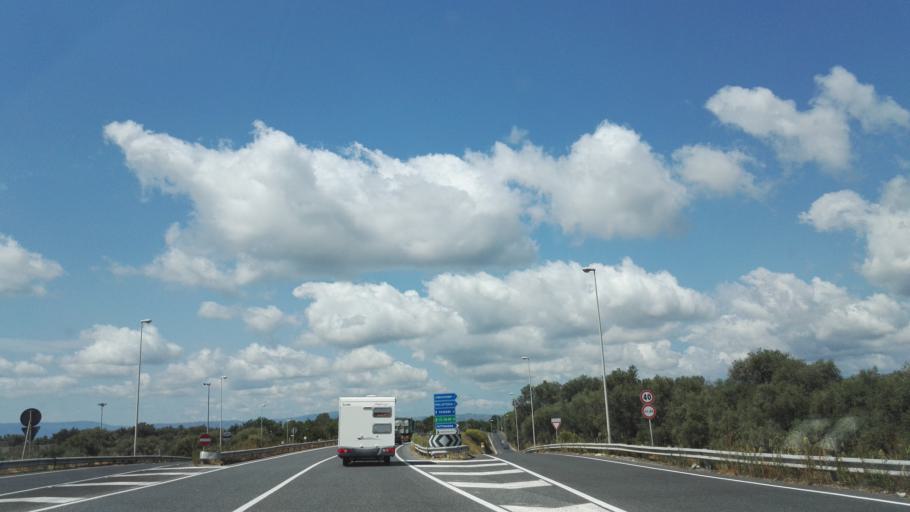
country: IT
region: Calabria
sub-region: Provincia di Reggio Calabria
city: Cinque Frondi
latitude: 38.4188
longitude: 16.0855
